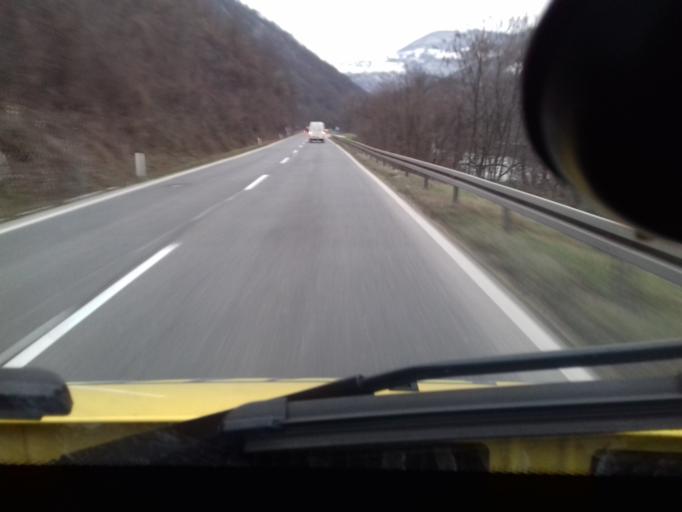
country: BA
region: Federation of Bosnia and Herzegovina
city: Lokvine
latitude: 44.2710
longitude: 17.8811
